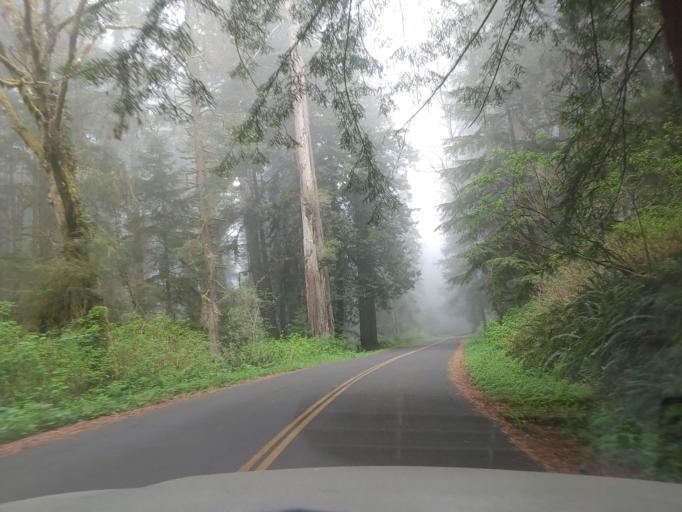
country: US
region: California
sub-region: Del Norte County
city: Bertsch-Oceanview
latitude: 41.4570
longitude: -124.0488
